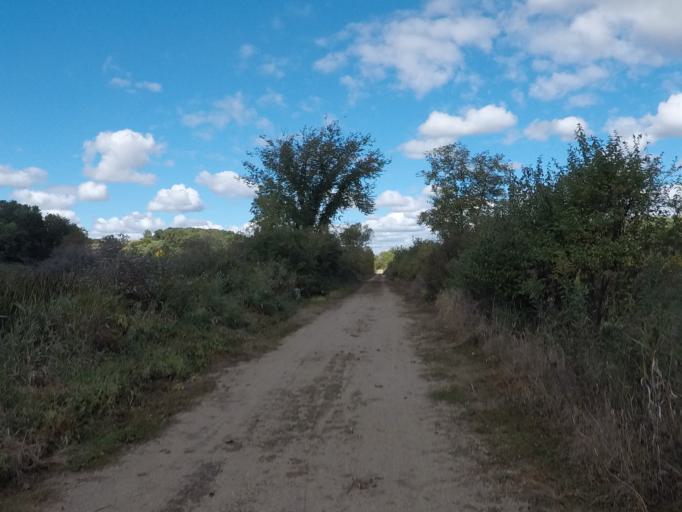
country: US
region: Wisconsin
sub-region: Richland County
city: Richland Center
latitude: 43.2709
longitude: -90.3090
